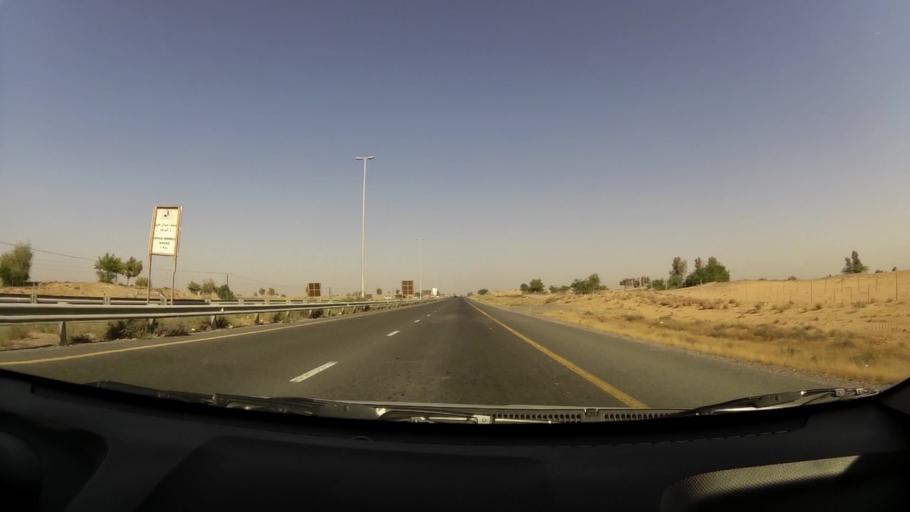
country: AE
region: Umm al Qaywayn
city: Umm al Qaywayn
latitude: 25.4654
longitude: 55.5949
